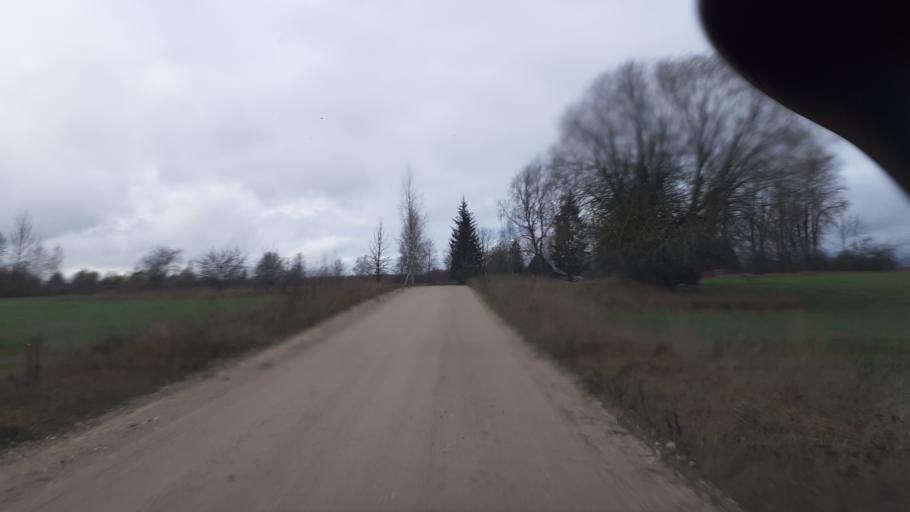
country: LV
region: Kuldigas Rajons
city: Kuldiga
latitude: 57.0427
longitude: 21.8742
